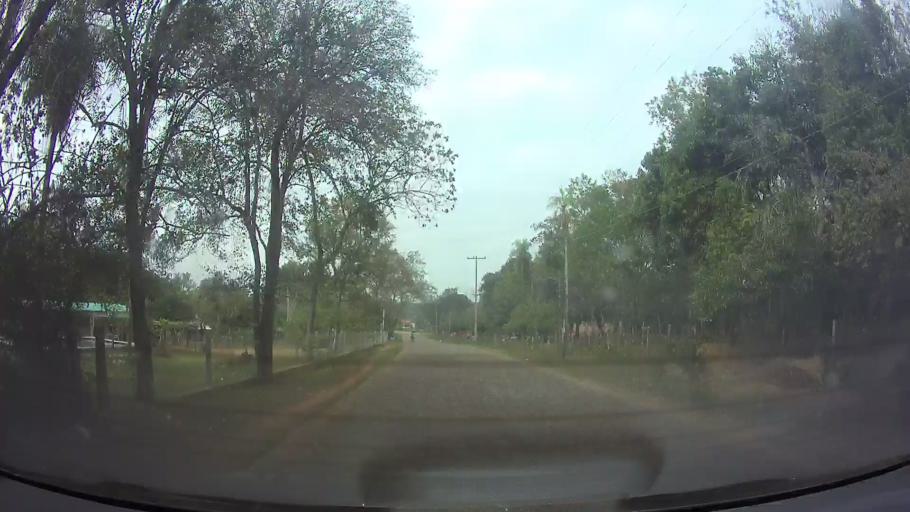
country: PY
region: Cordillera
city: Arroyos y Esteros
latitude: -25.0056
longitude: -57.1344
